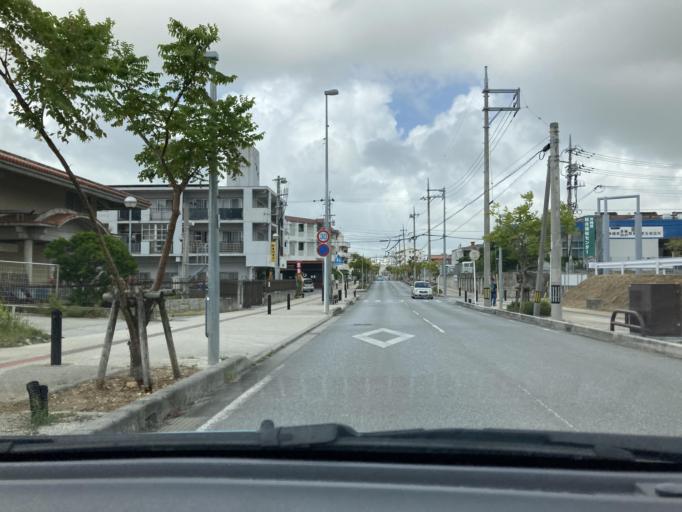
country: JP
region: Okinawa
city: Ginowan
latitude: 26.2311
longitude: 127.7332
